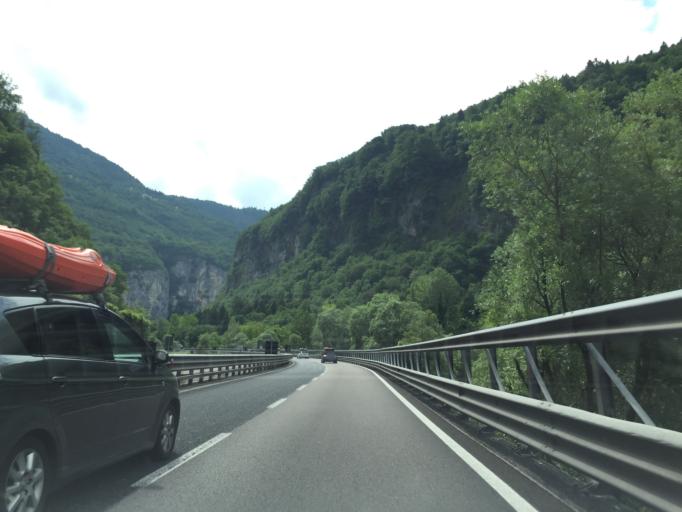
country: IT
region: Veneto
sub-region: Provincia di Vicenza
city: Enego
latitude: 45.9557
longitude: 11.7127
